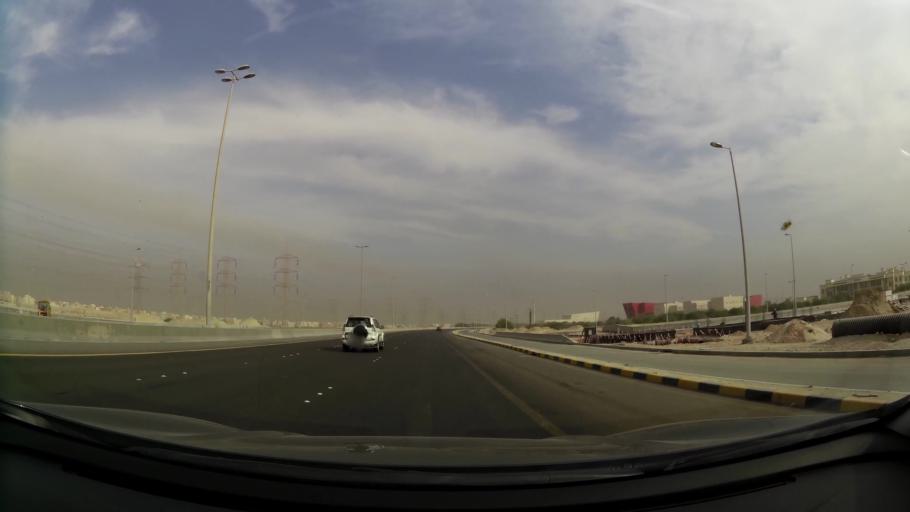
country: KW
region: Muhafazat al Jahra'
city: Al Jahra'
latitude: 29.3204
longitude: 47.7853
